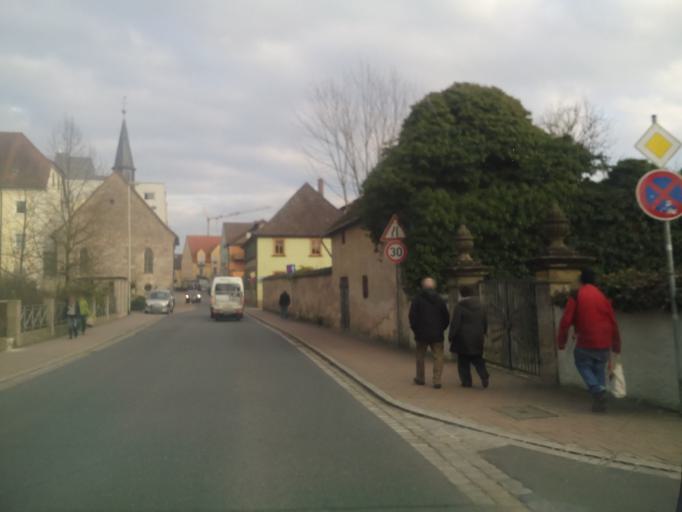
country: DE
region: Bavaria
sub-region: Regierungsbezirk Mittelfranken
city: Hochstadt an der Aisch
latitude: 49.7060
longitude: 10.8038
